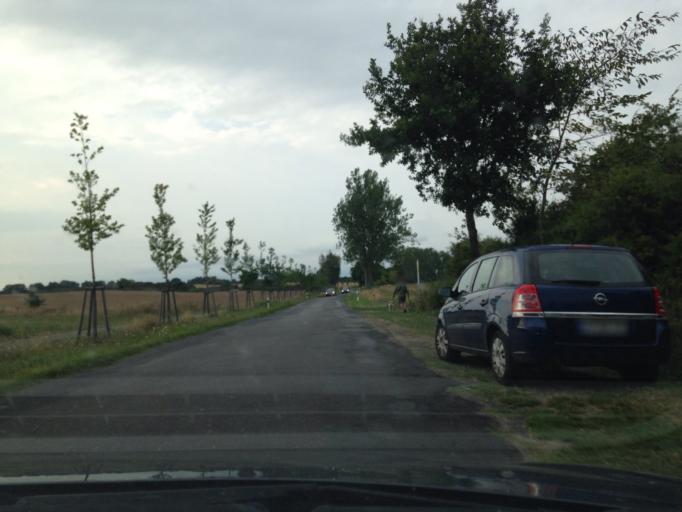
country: DE
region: Mecklenburg-Vorpommern
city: Loitz
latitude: 53.3056
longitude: 13.4218
